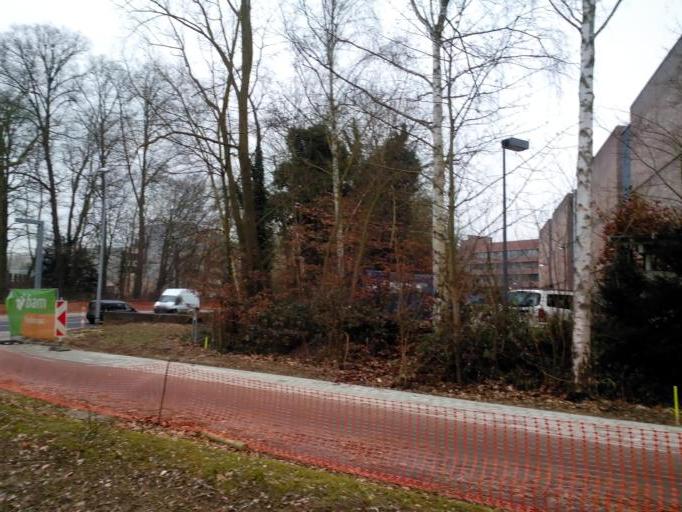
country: BE
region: Flanders
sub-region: Provincie Vlaams-Brabant
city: Leuven
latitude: 50.8653
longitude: 4.6809
